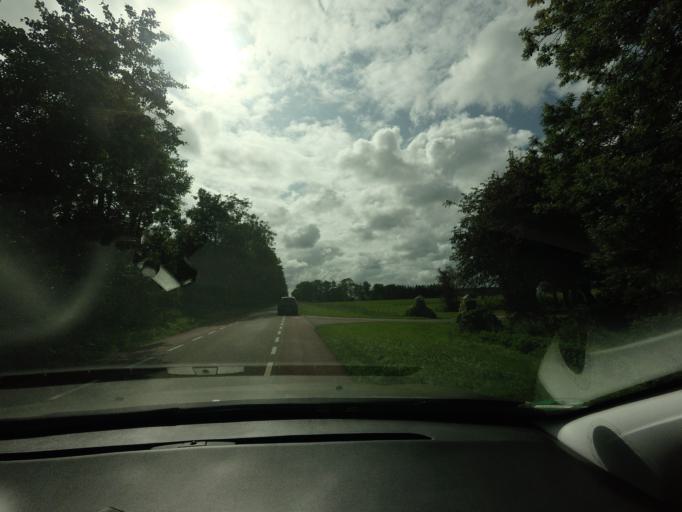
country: NL
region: North Holland
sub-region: Gemeente Medemblik
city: Medemblik
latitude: 52.8124
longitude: 5.1075
